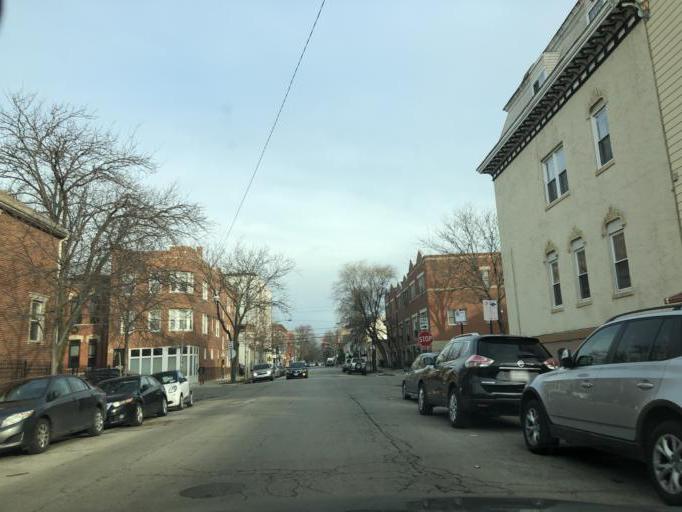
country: US
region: Illinois
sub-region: Cook County
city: Chicago
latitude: 41.8948
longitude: -87.6721
